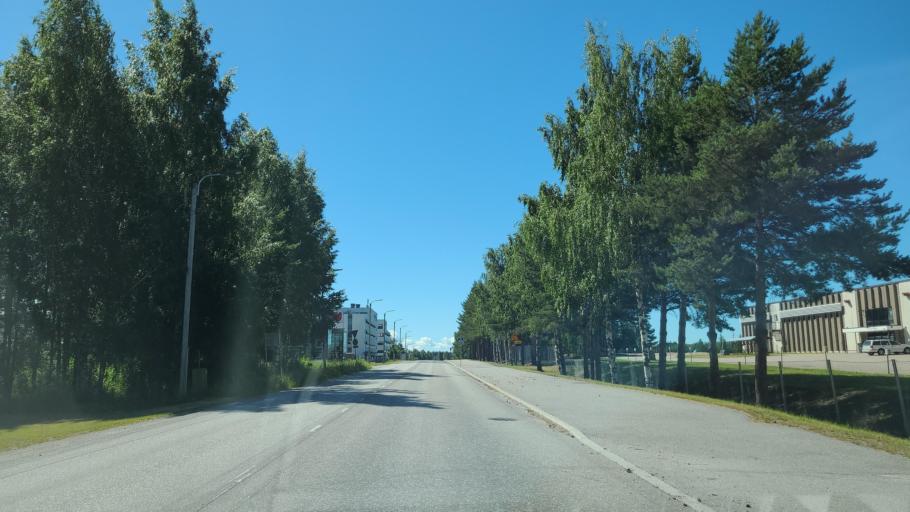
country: FI
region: Ostrobothnia
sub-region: Vaasa
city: Ristinummi
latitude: 63.0595
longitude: 21.7333
